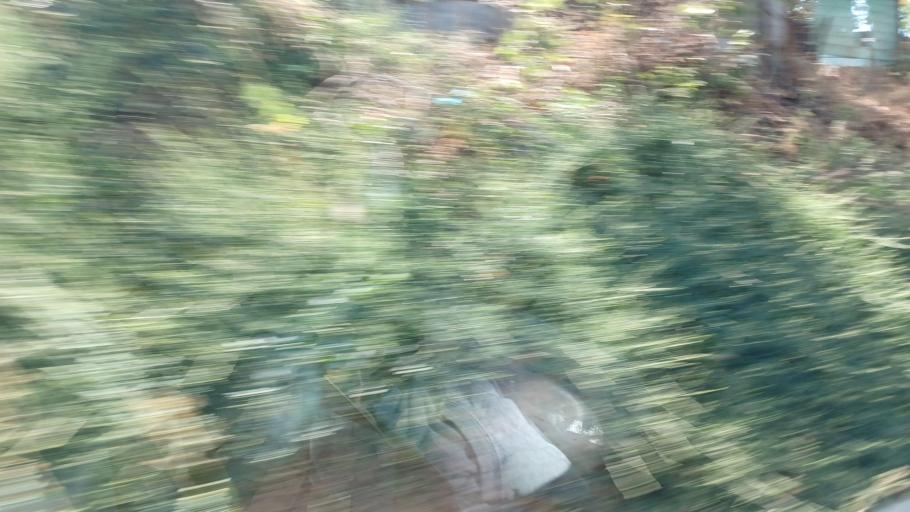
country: CY
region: Pafos
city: Mesogi
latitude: 34.8892
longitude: 32.6111
